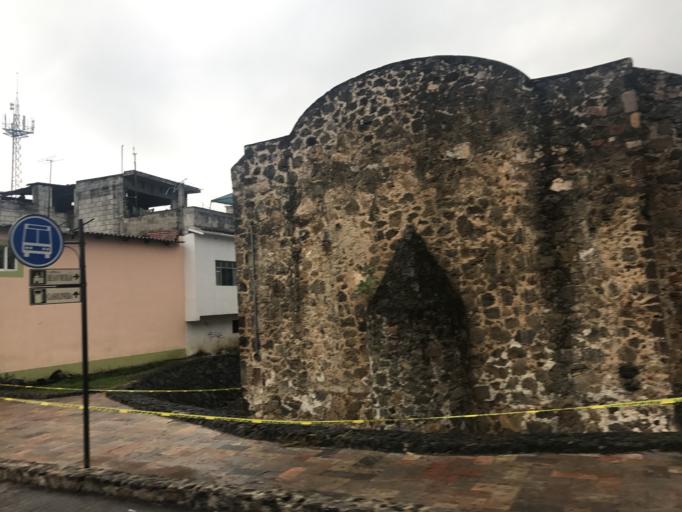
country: MX
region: Morelos
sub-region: Tlayacapan
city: Tlayacapan
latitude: 18.9579
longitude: -98.9798
